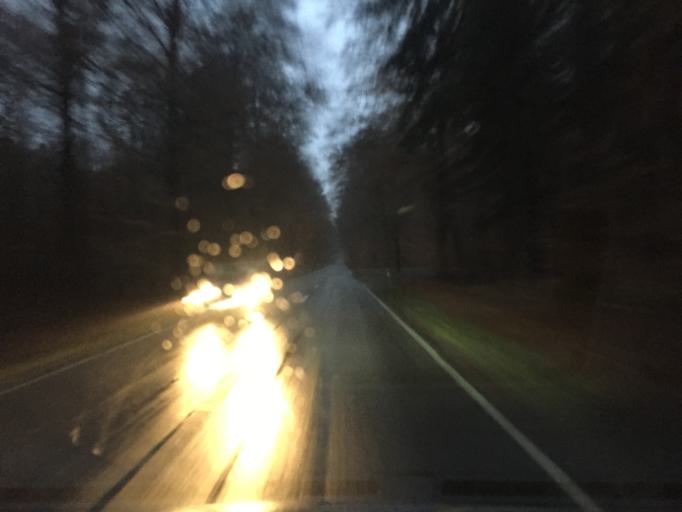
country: DE
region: Lower Saxony
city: Sudwalde
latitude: 52.8280
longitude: 8.8402
